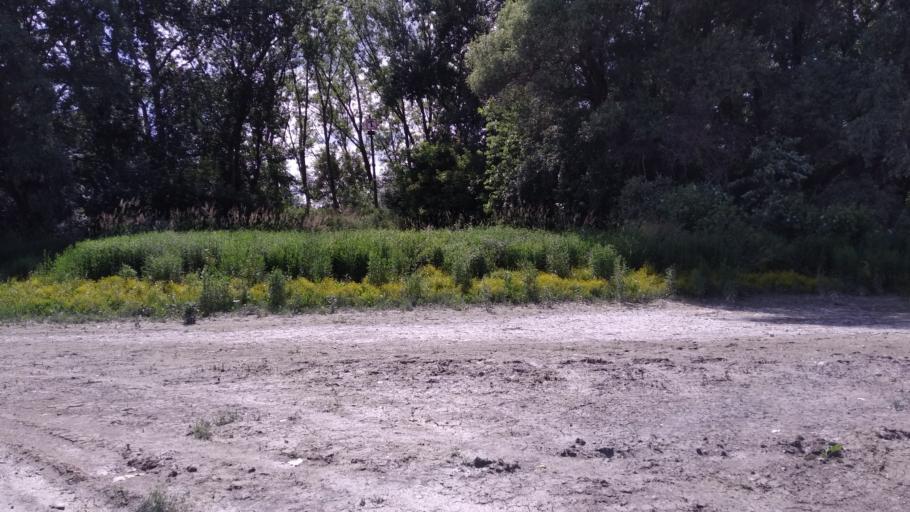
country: HU
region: Pest
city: Szentendre
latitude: 47.6334
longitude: 19.0852
